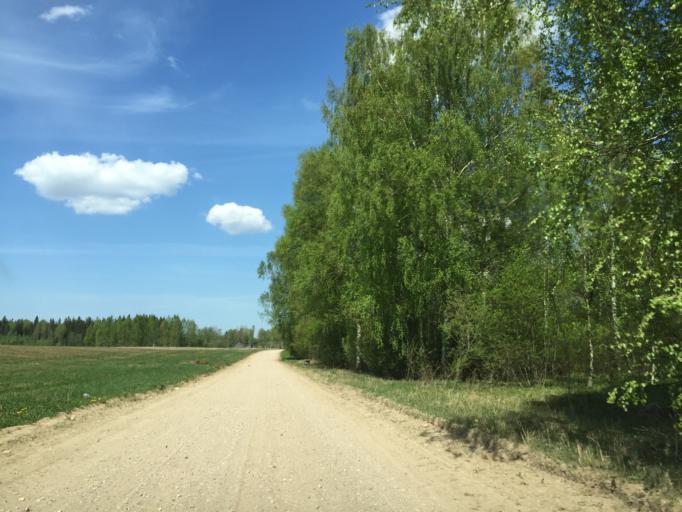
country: LV
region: Limbazu Rajons
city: Limbazi
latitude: 57.3607
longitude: 24.6401
